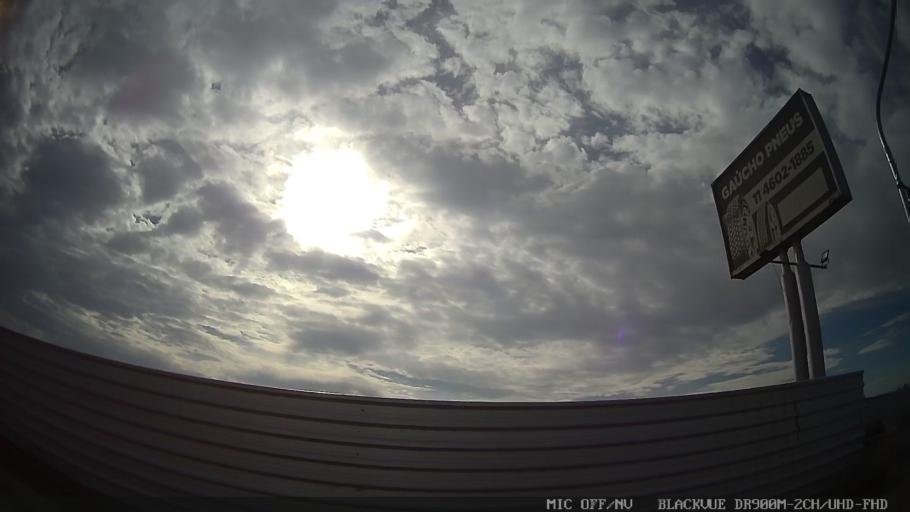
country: BR
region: Sao Paulo
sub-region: Salto
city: Salto
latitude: -23.1798
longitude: -47.2677
